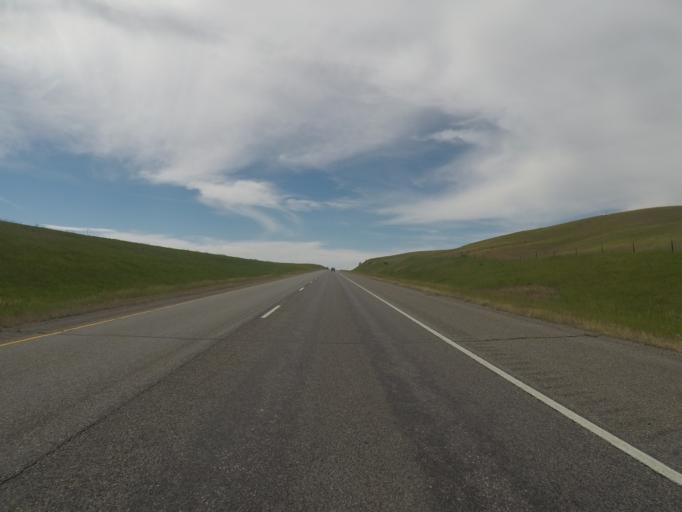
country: US
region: Montana
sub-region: Stillwater County
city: Columbus
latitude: 45.6131
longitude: -109.1738
